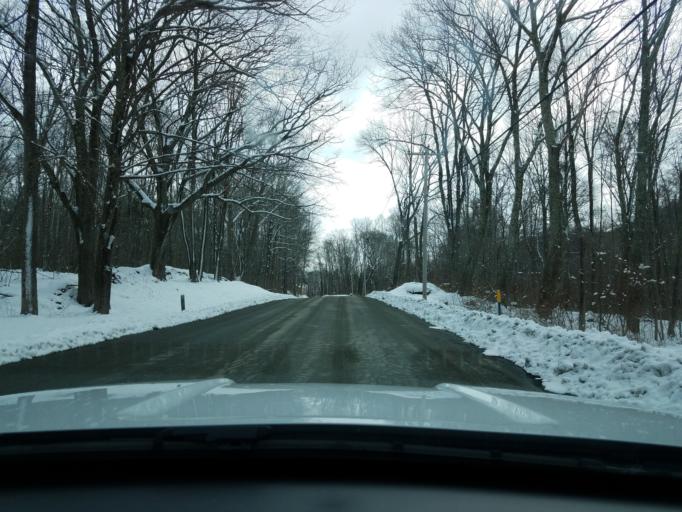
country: US
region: Connecticut
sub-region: Litchfield County
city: Kent
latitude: 41.7674
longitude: -73.4173
